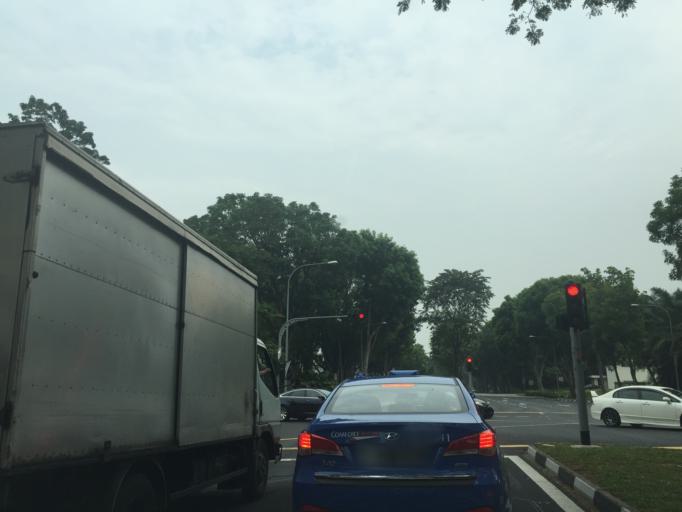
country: SG
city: Singapore
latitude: 1.3683
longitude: 103.8284
